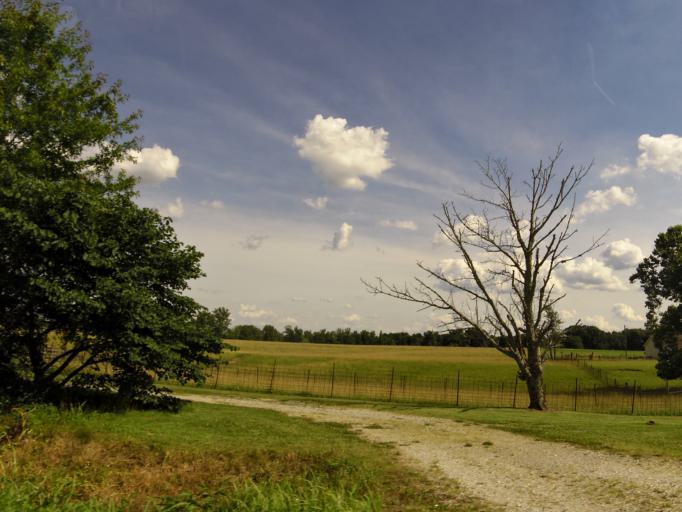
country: US
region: Tennessee
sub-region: Gibson County
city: Milan
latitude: 35.9815
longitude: -88.6196
